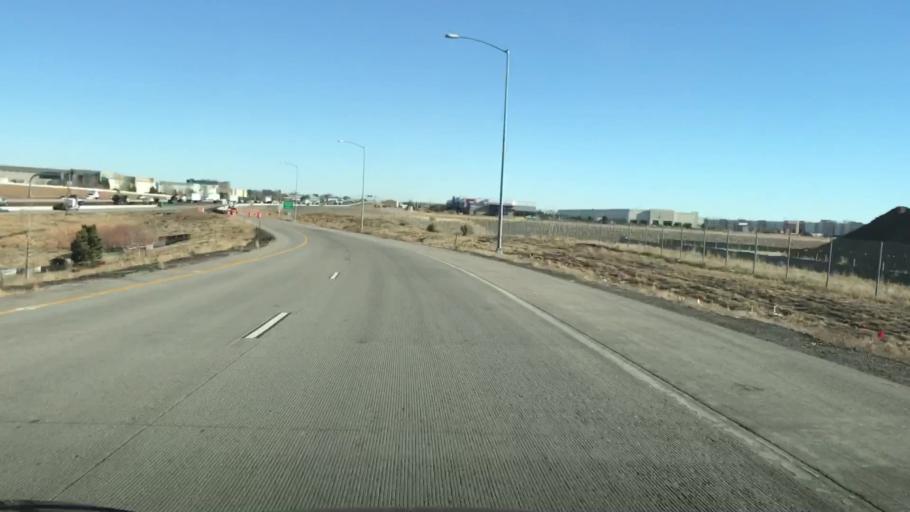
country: US
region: Colorado
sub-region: Adams County
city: Commerce City
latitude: 39.7761
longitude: -104.8819
